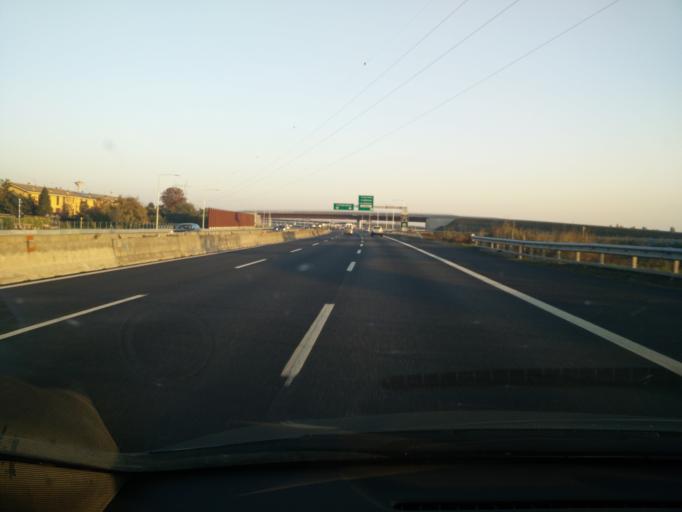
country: IT
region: Lombardy
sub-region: Citta metropolitana di Milano
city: Riozzo
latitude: 45.3427
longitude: 9.3180
